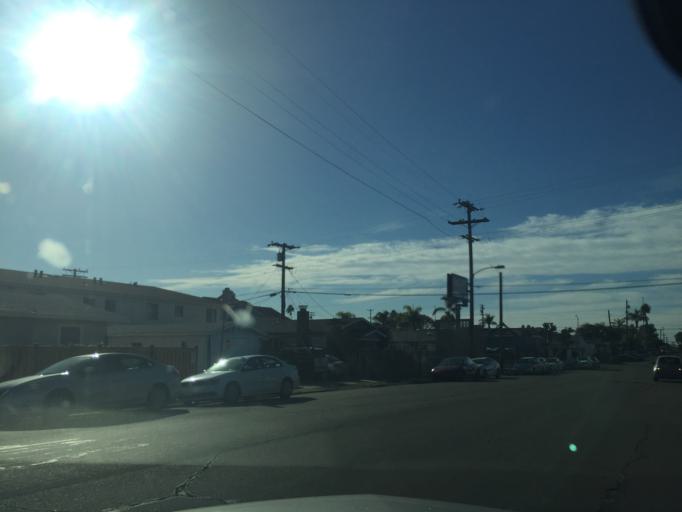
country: US
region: California
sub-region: San Diego County
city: San Diego
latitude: 32.7523
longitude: -117.1290
